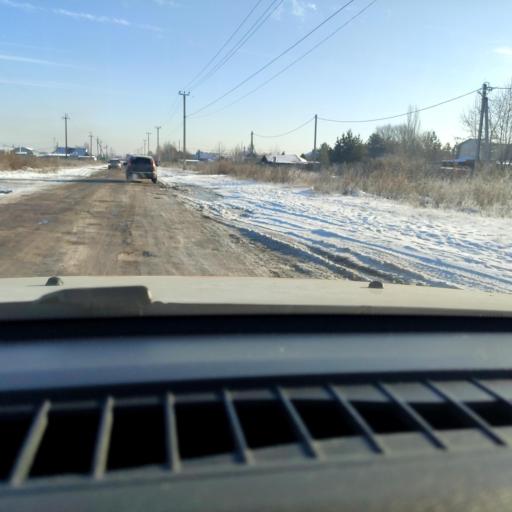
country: RU
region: Samara
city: Podstepki
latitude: 53.5193
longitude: 49.1331
